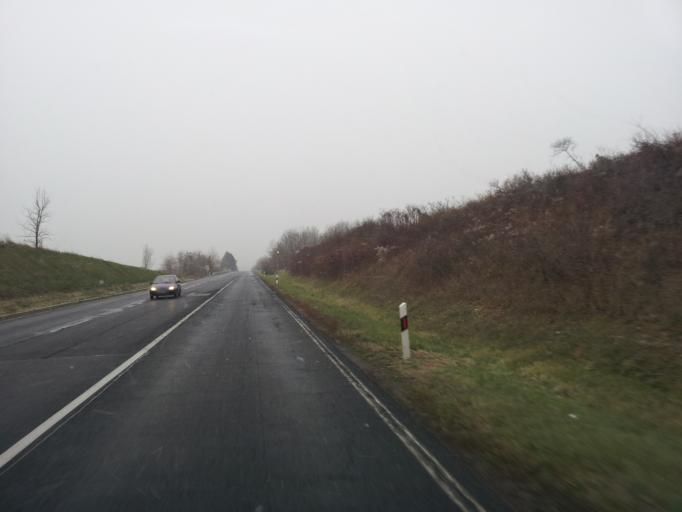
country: HU
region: Veszprem
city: Urkut
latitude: 47.1445
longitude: 17.6802
